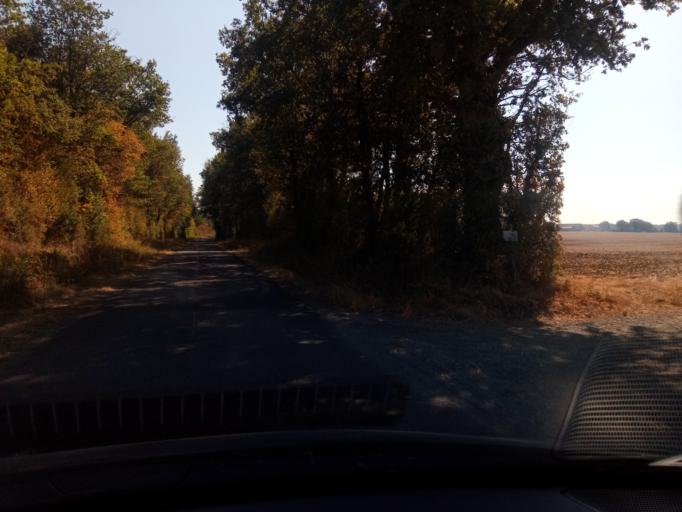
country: FR
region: Poitou-Charentes
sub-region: Departement de la Vienne
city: Lussac-les-Chateaux
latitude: 46.3813
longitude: 0.7900
